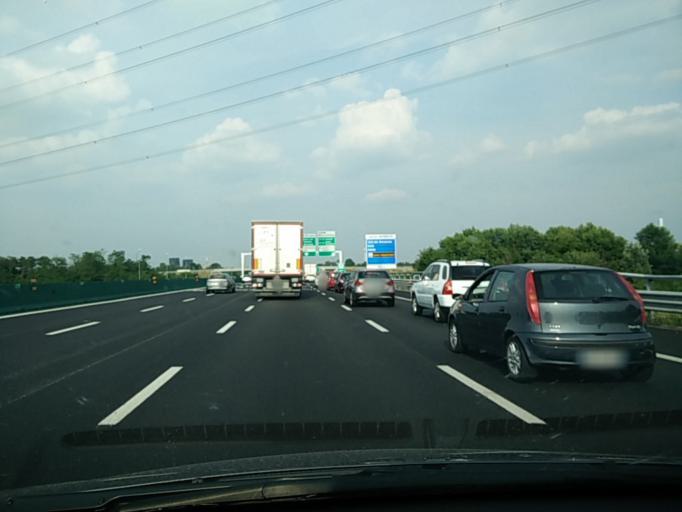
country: IT
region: Lombardy
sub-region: Citta metropolitana di Milano
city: Rho
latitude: 45.5111
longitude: 9.0510
